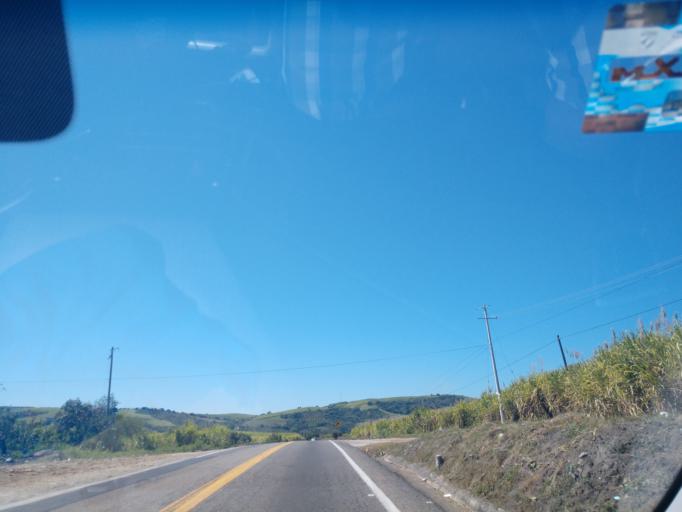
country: MX
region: Nayarit
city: Xalisco
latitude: 21.3716
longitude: -104.9058
